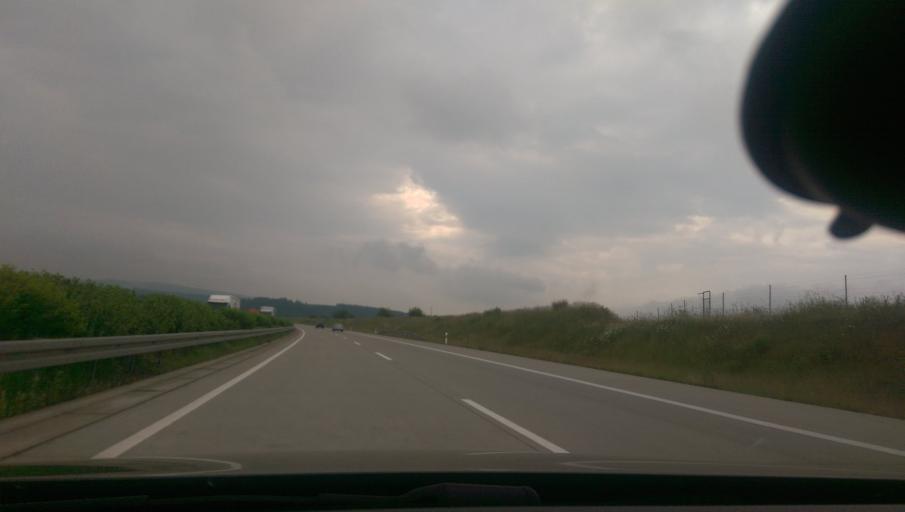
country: DE
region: Thuringia
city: Reinholterode
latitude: 51.4047
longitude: 10.1982
